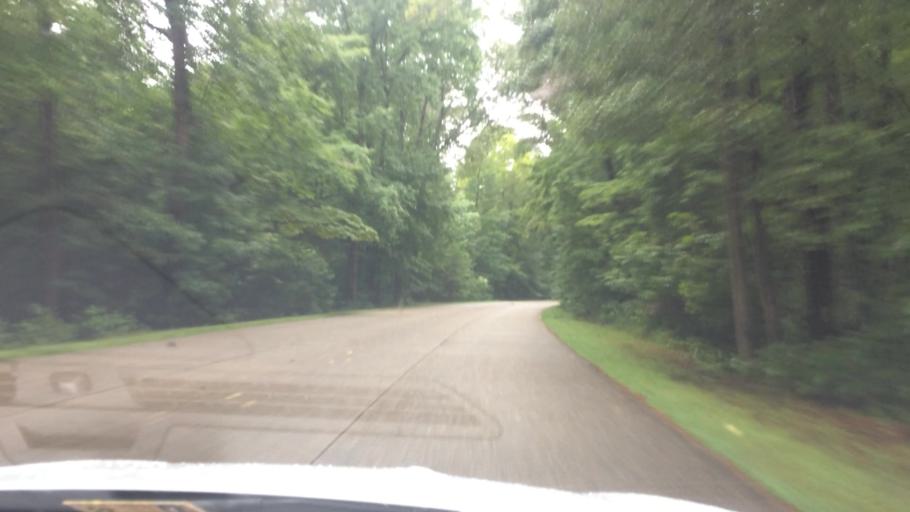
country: US
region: Virginia
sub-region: City of Williamsburg
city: Williamsburg
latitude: 37.2817
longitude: -76.6502
